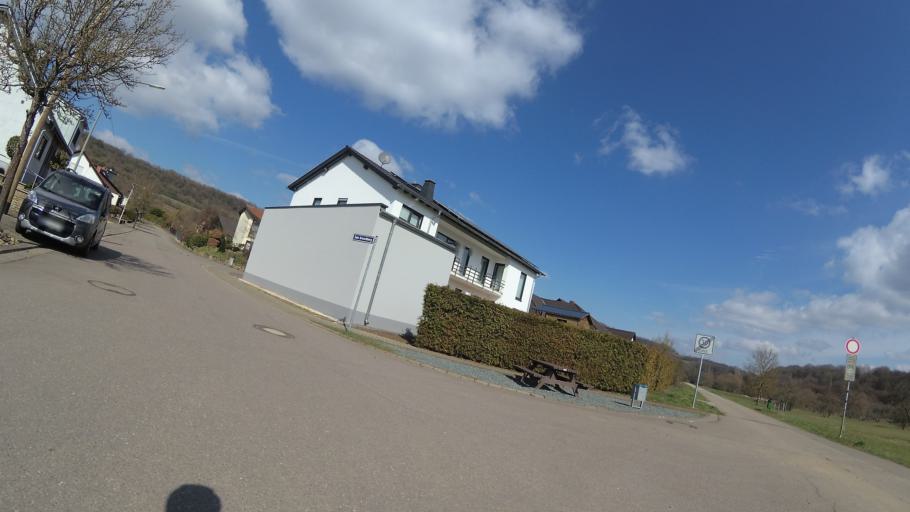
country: DE
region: Saarland
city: Rehlingen-Siersburg
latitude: 49.3598
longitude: 6.6250
